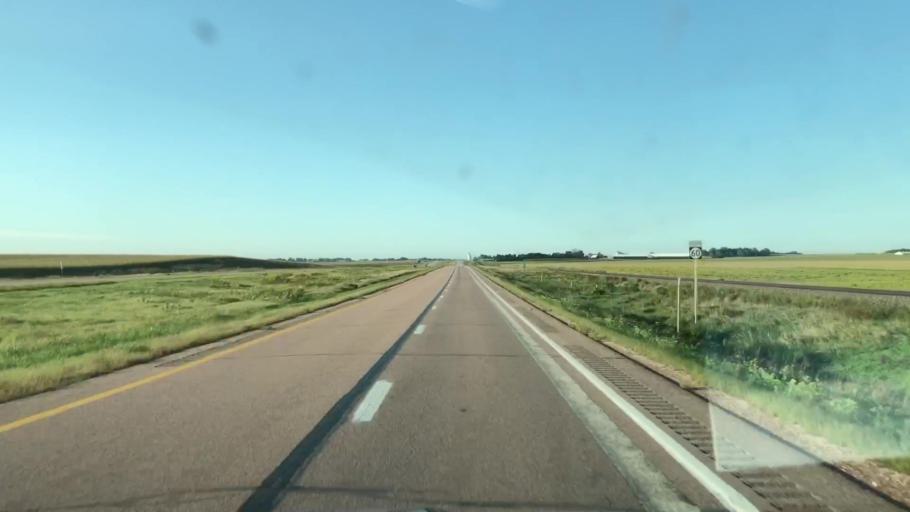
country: US
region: Iowa
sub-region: Osceola County
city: Sibley
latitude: 43.3601
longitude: -95.7678
